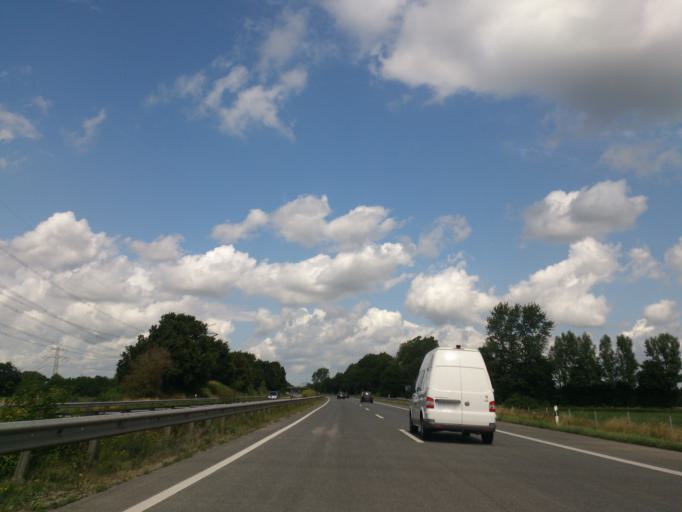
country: DE
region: Schleswig-Holstein
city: Klein Offenseth-Sparrieshoop
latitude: 53.7896
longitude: 9.6996
